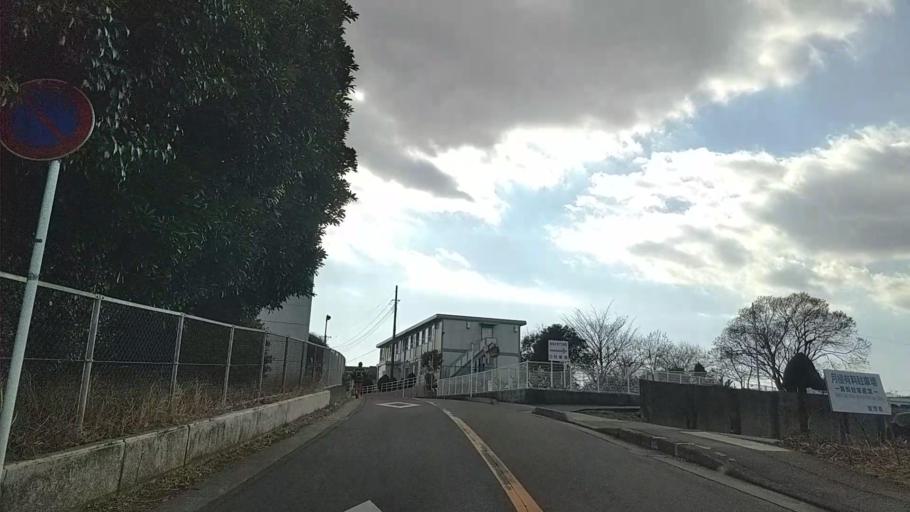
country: JP
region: Kanagawa
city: Isehara
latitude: 35.4074
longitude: 139.3132
